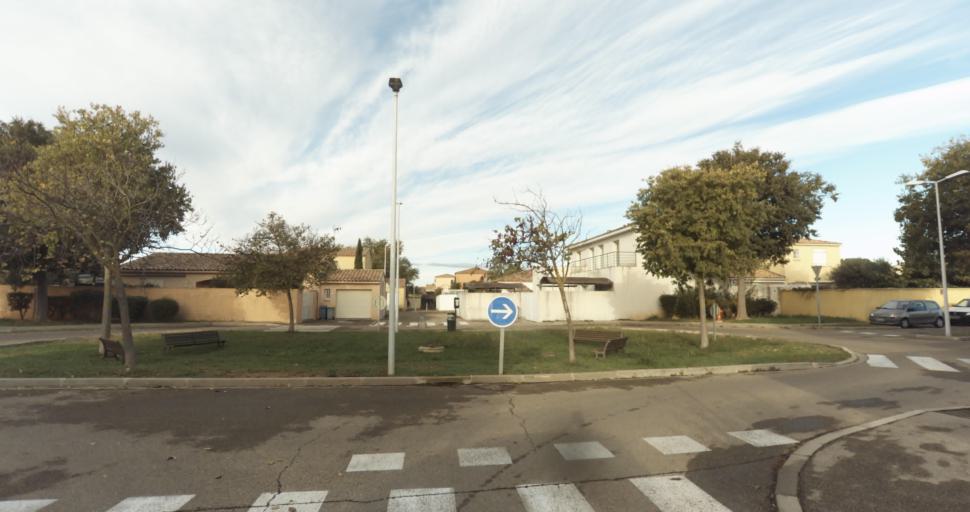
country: FR
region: Languedoc-Roussillon
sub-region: Departement du Gard
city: Aigues-Mortes
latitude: 43.5645
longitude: 4.2056
